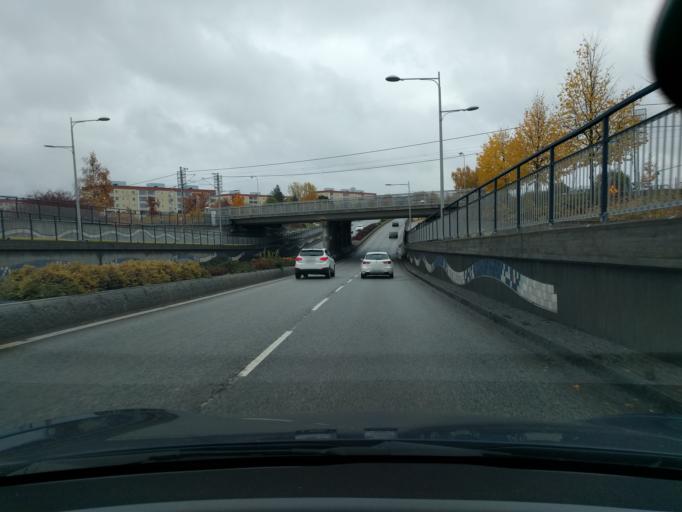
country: SE
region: Stockholm
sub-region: Taby Kommun
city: Taby
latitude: 59.4481
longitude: 18.0925
